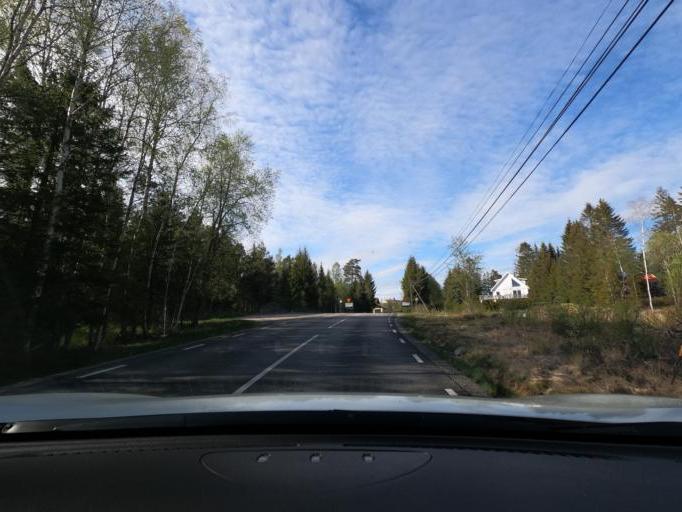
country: SE
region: Vaestra Goetaland
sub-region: Harryda Kommun
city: Landvetter
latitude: 57.6672
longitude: 12.2437
